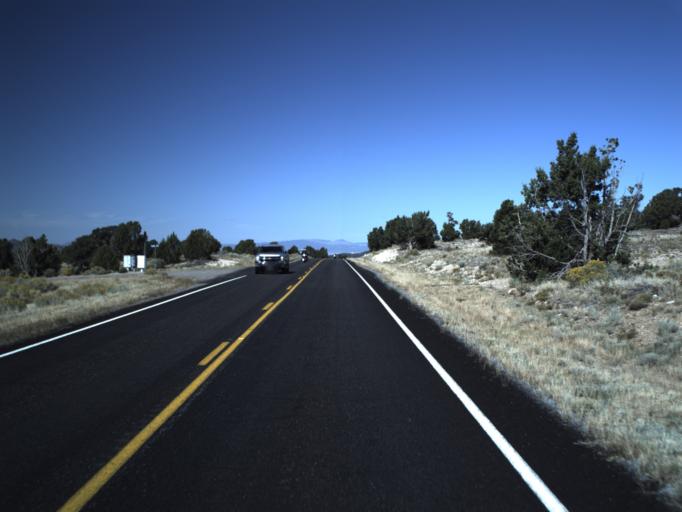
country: US
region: Utah
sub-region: Washington County
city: Enterprise
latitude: 37.6147
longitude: -113.4069
